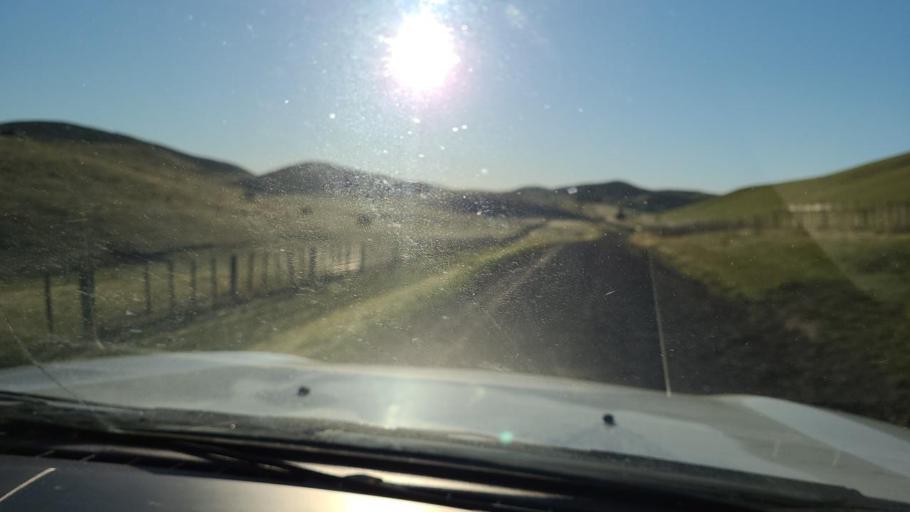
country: NZ
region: Hawke's Bay
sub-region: Hastings District
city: Hastings
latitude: -39.5886
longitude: 176.6627
